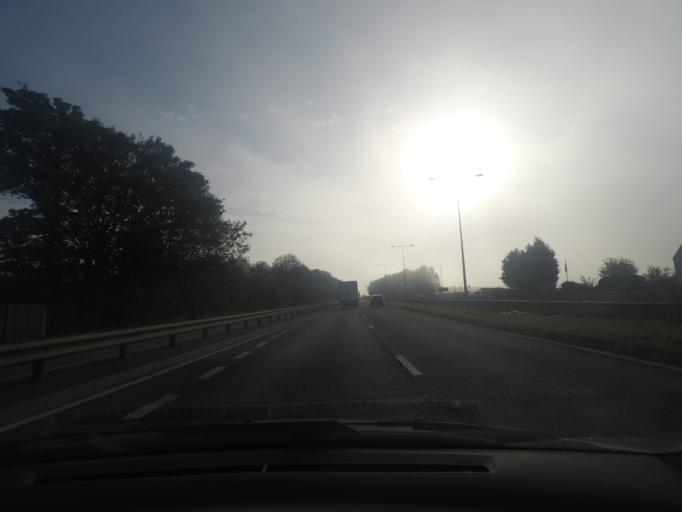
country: GB
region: England
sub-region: East Riding of Yorkshire
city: Welton
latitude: 53.7304
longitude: -0.5488
